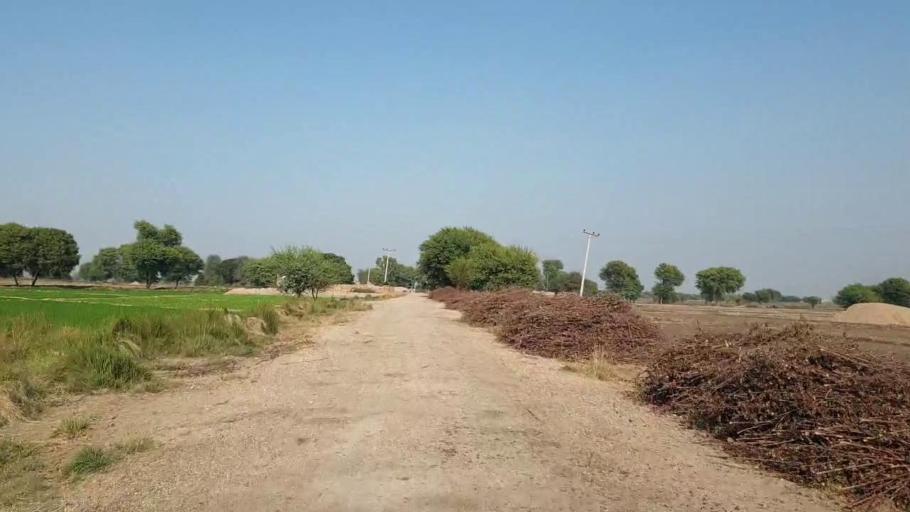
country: PK
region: Sindh
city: Sehwan
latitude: 26.4600
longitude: 67.8155
